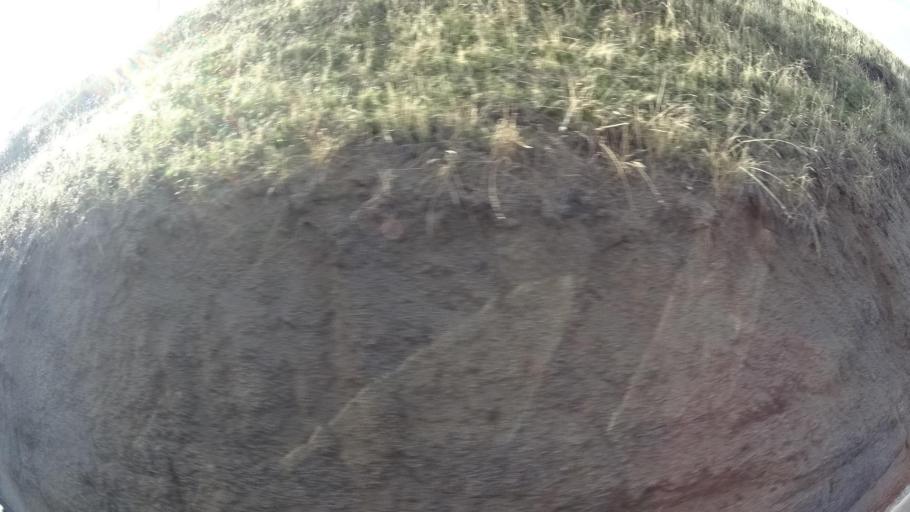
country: US
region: California
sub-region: Kern County
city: Oildale
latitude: 35.6202
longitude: -118.8551
